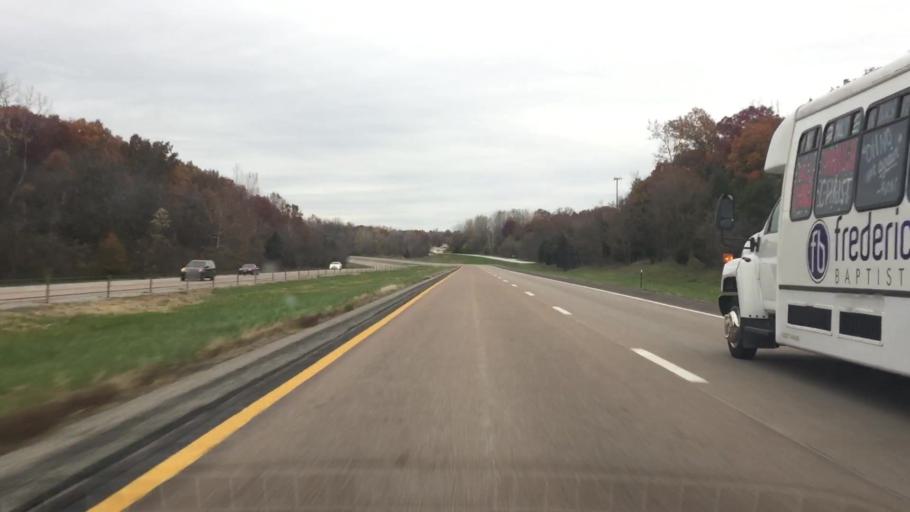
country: US
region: Missouri
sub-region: Cole County
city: Jefferson City
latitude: 38.6648
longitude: -92.2268
